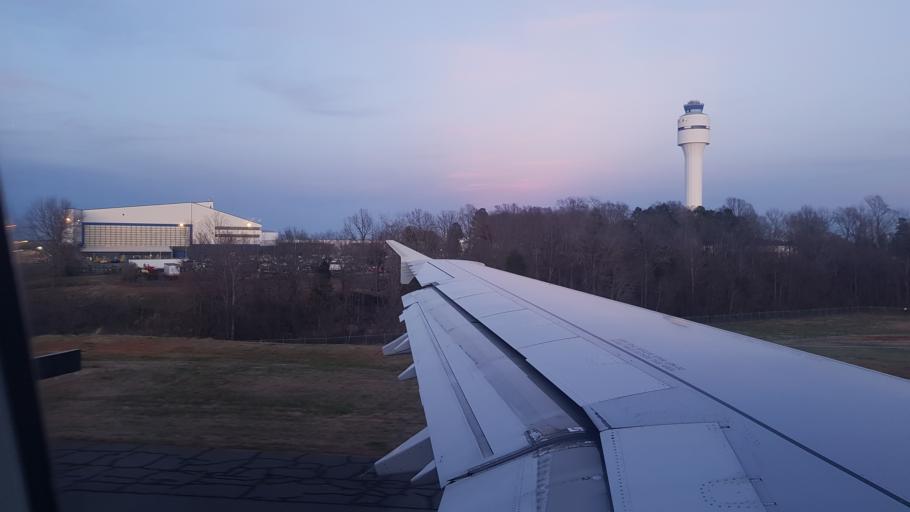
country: US
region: North Carolina
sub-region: Gaston County
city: Belmont
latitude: 35.2044
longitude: -80.9491
